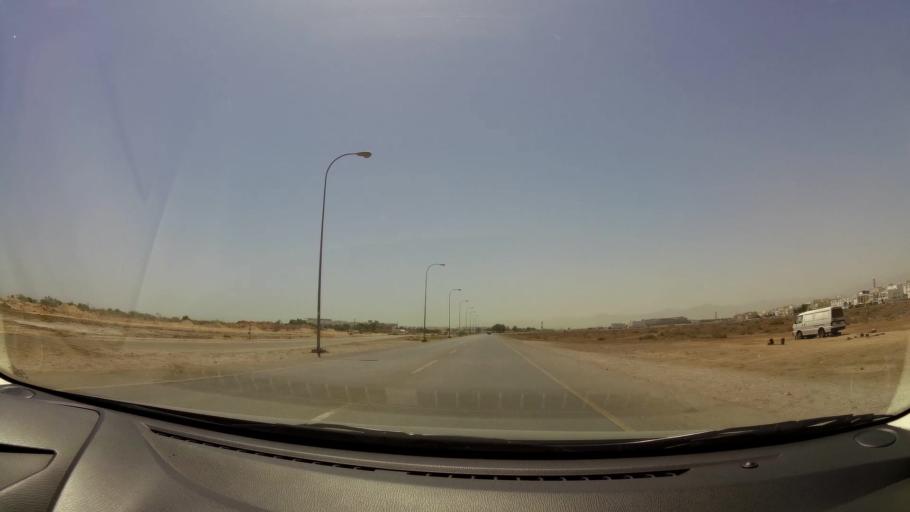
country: OM
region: Muhafazat Masqat
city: As Sib al Jadidah
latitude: 23.6291
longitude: 58.2548
